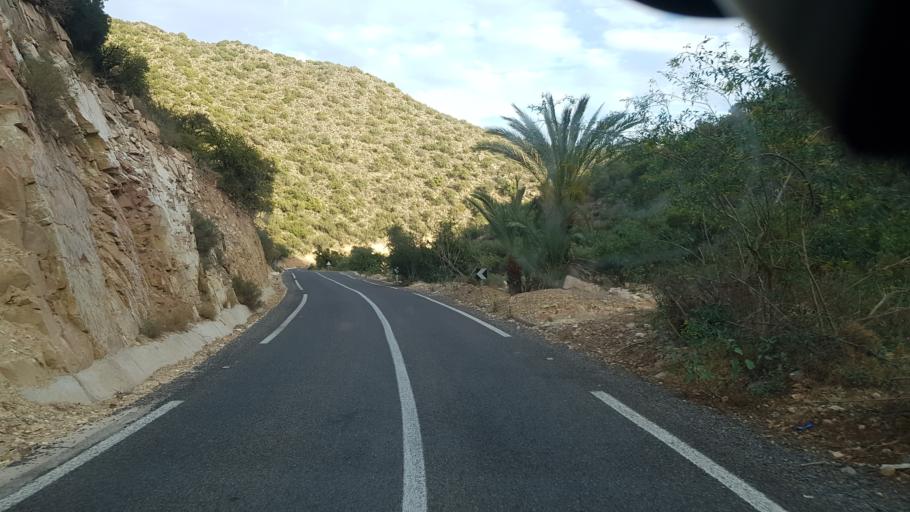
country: MA
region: Souss-Massa-Draa
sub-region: Agadir-Ida-ou-Tnan
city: Aourir
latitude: 30.4988
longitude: -9.6079
